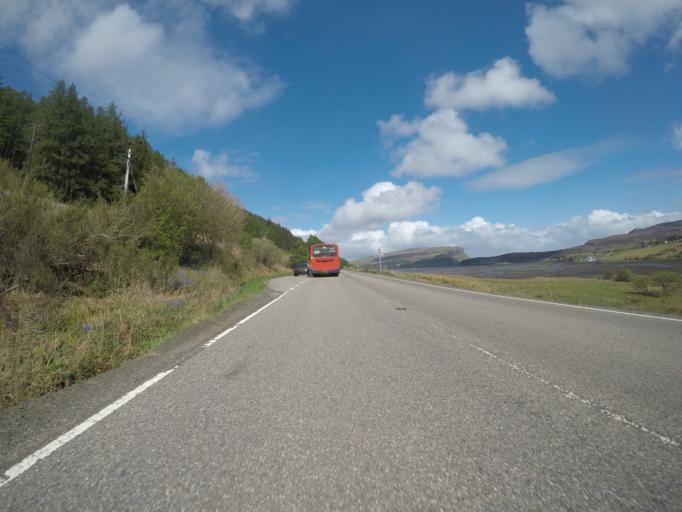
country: GB
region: Scotland
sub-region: Highland
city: Portree
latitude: 57.3921
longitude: -6.2048
